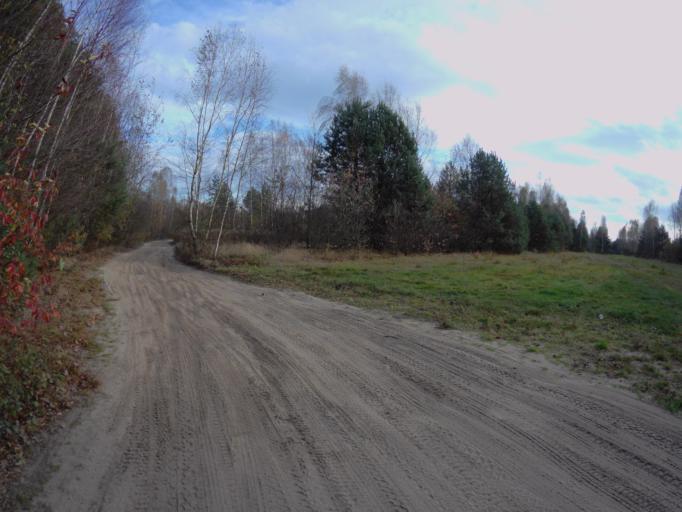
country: PL
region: Subcarpathian Voivodeship
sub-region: Powiat kolbuszowski
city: Lipnica
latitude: 50.3258
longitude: 21.9368
